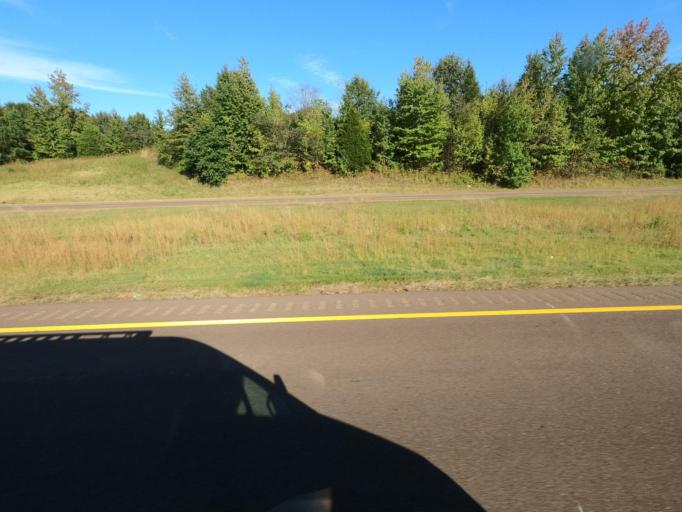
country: US
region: Tennessee
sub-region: Dyer County
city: Dyersburg
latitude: 35.9775
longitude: -89.3409
